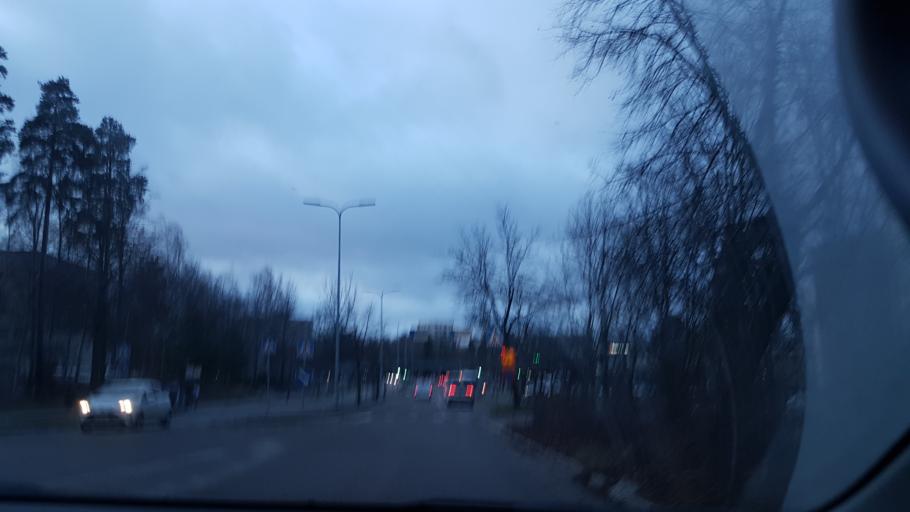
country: FI
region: Uusimaa
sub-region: Helsinki
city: Vantaa
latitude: 60.2793
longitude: 25.1080
